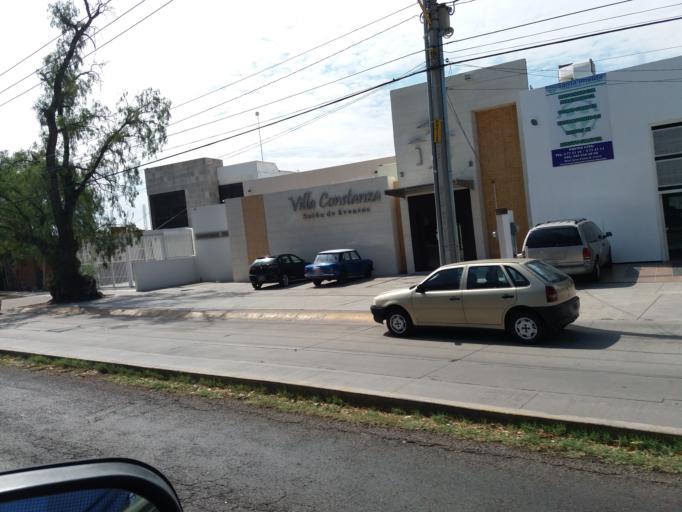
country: MX
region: Aguascalientes
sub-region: Aguascalientes
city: La Loma de los Negritos
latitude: 21.8695
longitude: -102.3252
